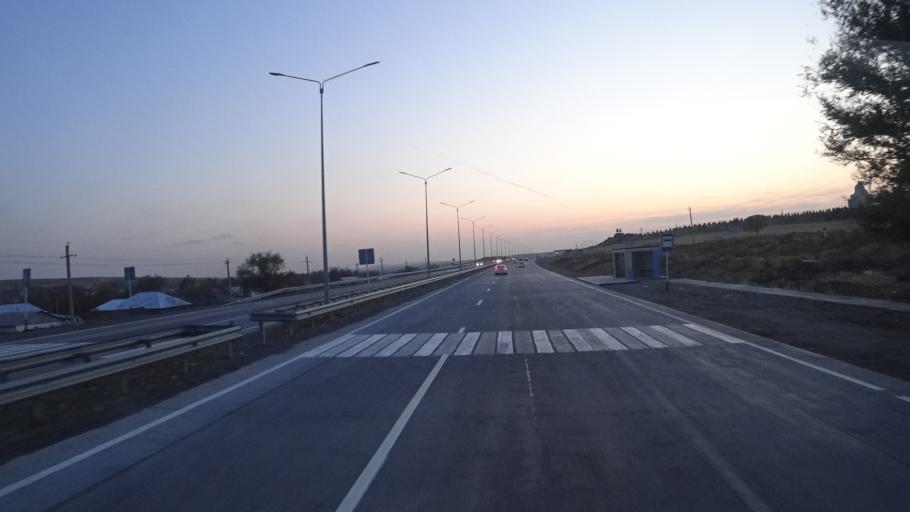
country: KZ
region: Ongtustik Qazaqstan
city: Qazyqurt
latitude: 41.8776
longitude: 69.4330
